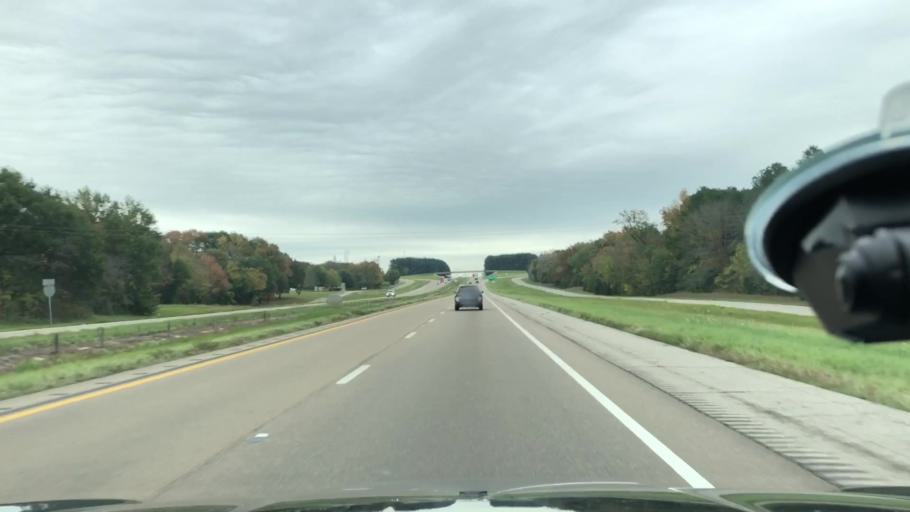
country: US
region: Texas
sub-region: Titus County
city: Mount Pleasant
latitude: 33.1595
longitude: -95.0841
